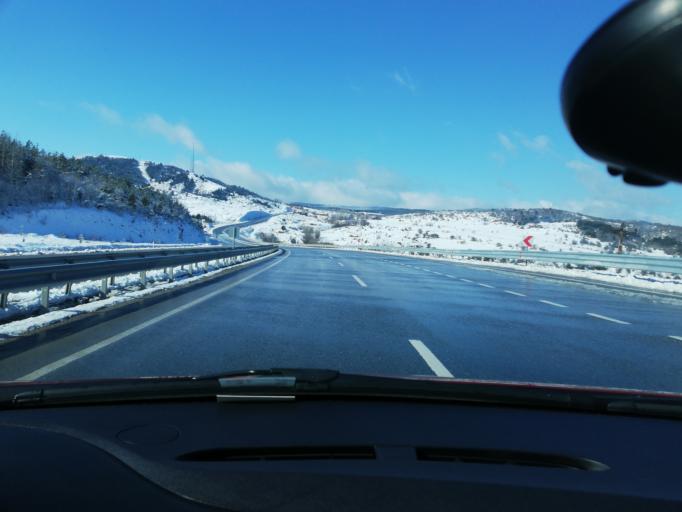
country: TR
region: Kastamonu
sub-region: Cide
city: Kastamonu
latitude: 41.3603
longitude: 33.6806
